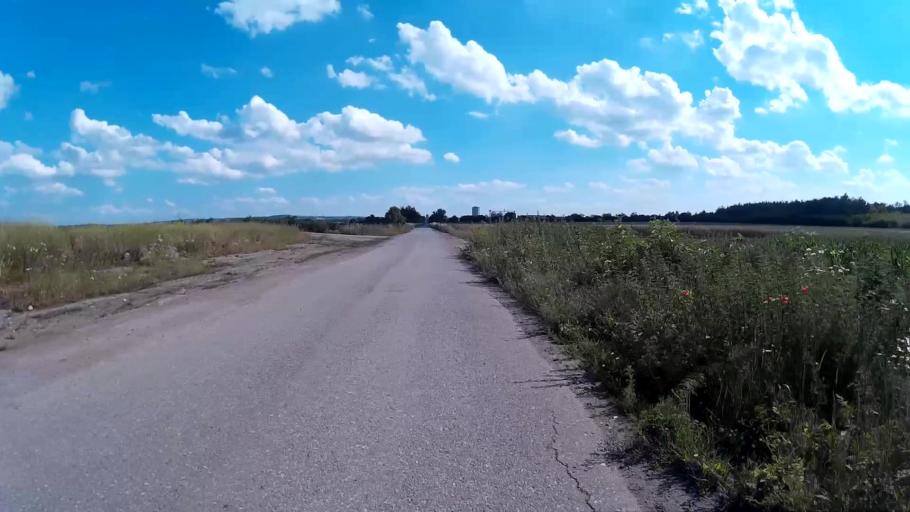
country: CZ
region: South Moravian
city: Menin
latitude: 49.0665
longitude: 16.7066
